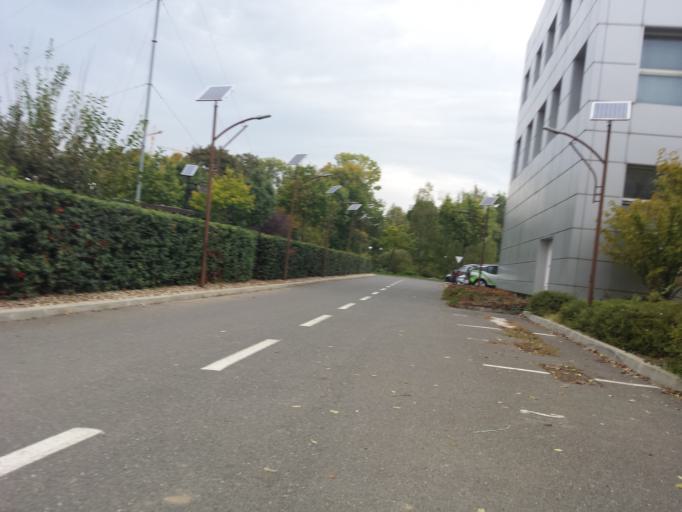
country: RO
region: Bucuresti
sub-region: Municipiul Bucuresti
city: Bucuresti
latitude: 44.4698
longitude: 26.0673
